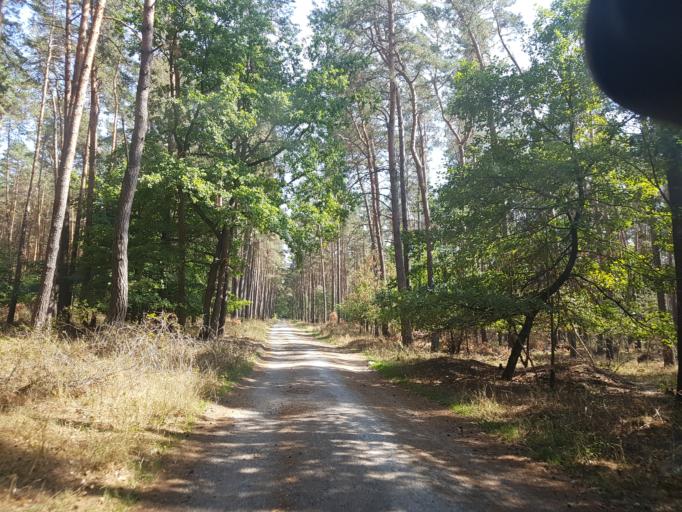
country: DE
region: Saxony-Anhalt
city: Coswig
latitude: 51.9737
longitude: 12.4610
